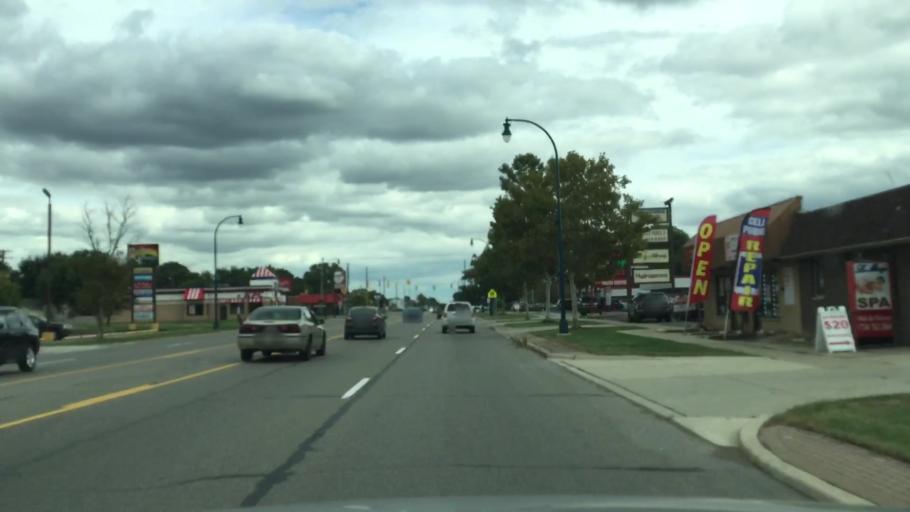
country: US
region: Michigan
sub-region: Wayne County
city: Garden City
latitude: 42.3258
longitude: -83.3234
